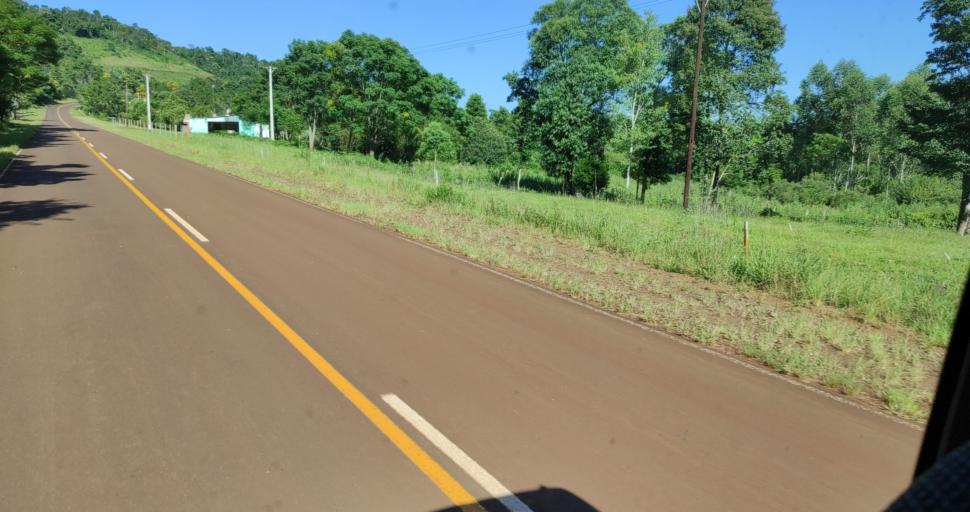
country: AR
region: Misiones
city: El Soberbio
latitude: -27.2245
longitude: -54.0562
